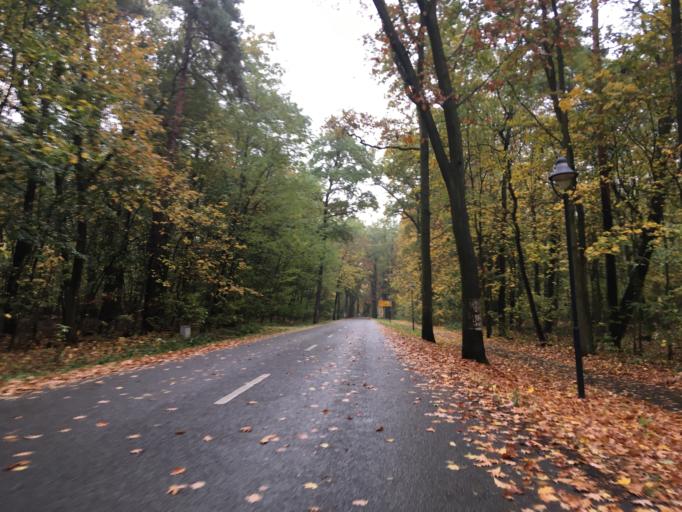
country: DE
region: Brandenburg
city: Beeskow
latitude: 52.1639
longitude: 14.2334
